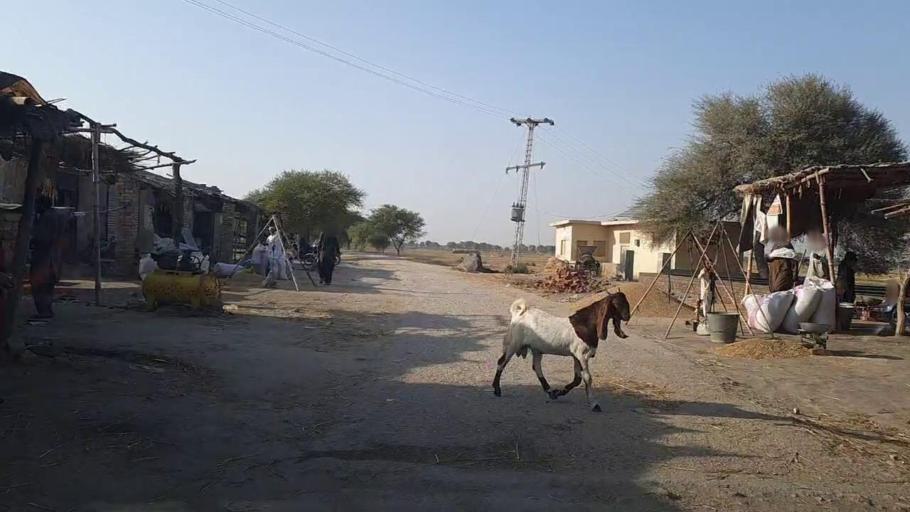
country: PK
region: Sindh
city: Kashmor
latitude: 28.4023
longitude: 69.4186
